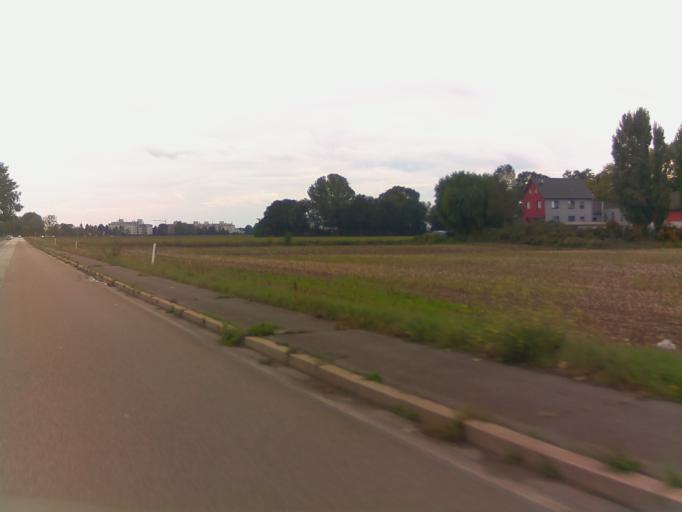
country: DE
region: Baden-Wuerttemberg
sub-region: Karlsruhe Region
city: Heddesheim
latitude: 49.5253
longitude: 8.6166
